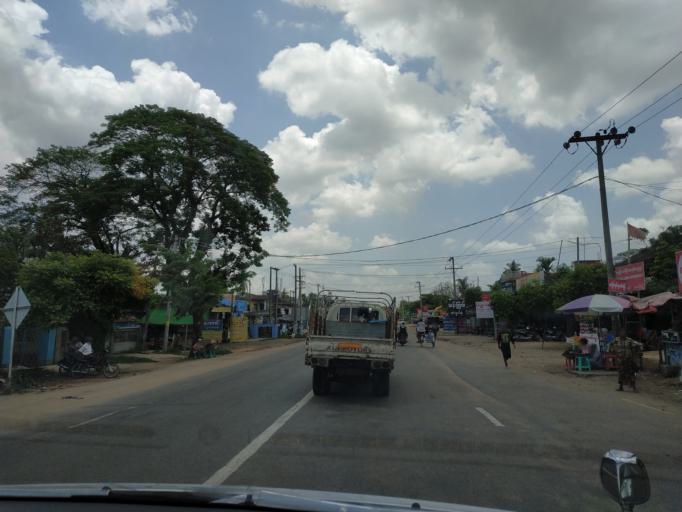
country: MM
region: Bago
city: Bago
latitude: 17.4742
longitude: 96.5283
